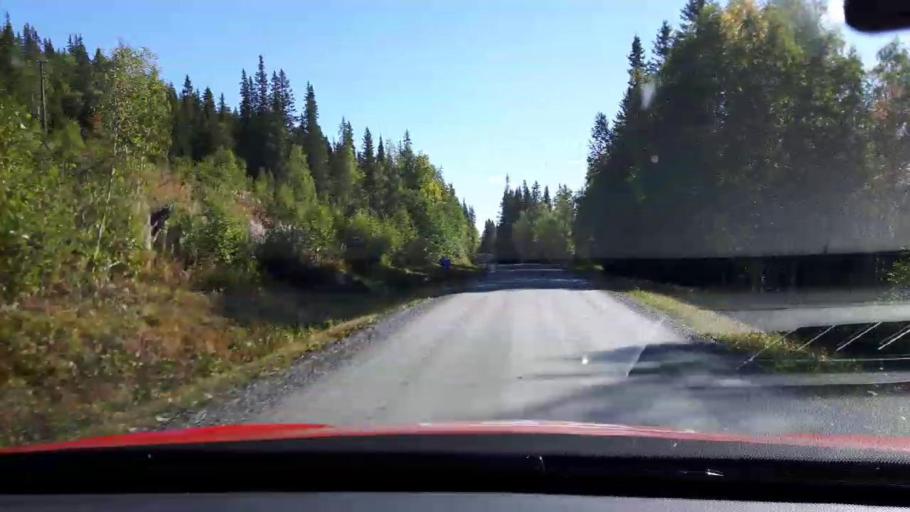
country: NO
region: Nord-Trondelag
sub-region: Lierne
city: Sandvika
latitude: 64.6418
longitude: 13.8001
